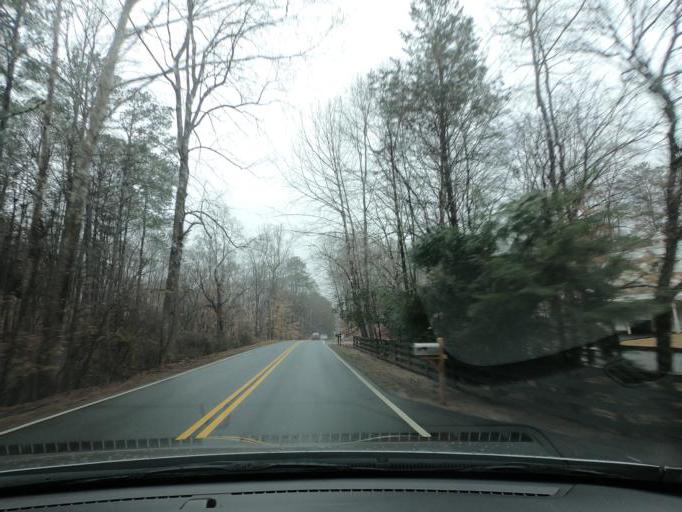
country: US
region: Georgia
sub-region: Fulton County
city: Milton
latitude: 34.1093
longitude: -84.3178
